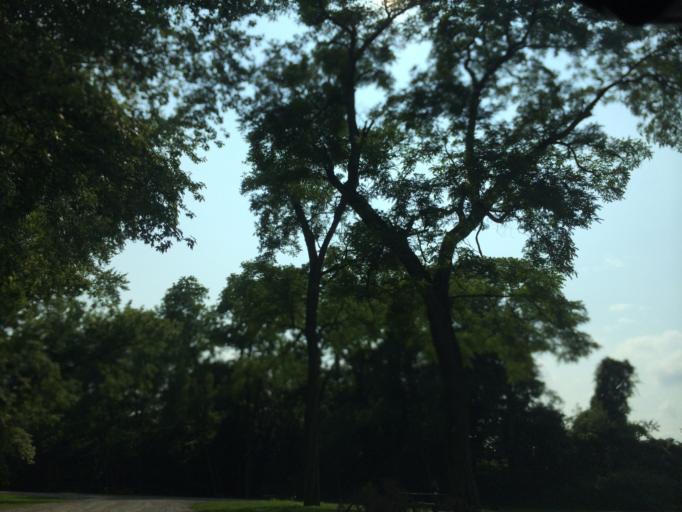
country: US
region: Pennsylvania
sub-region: Snyder County
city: Shamokin Dam
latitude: 40.8504
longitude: -76.8129
